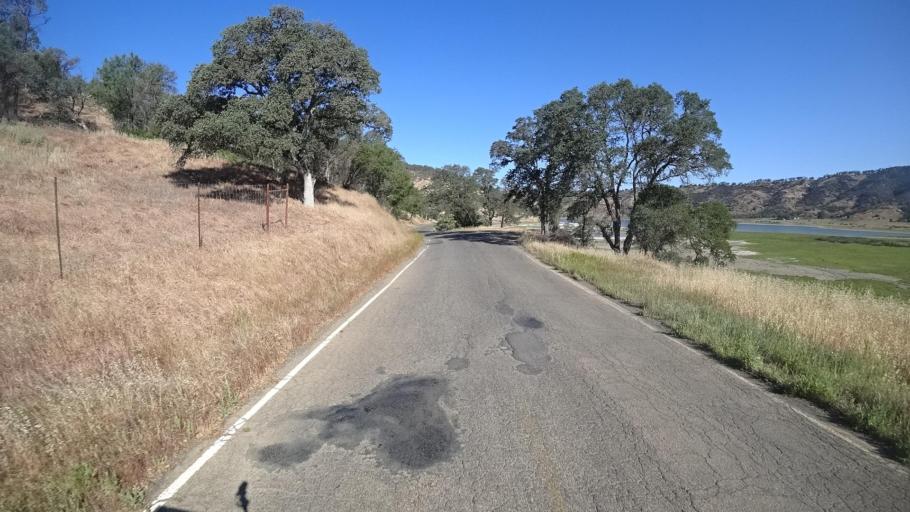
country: US
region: California
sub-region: Lake County
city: Clearlake Oaks
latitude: 38.9802
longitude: -122.6721
